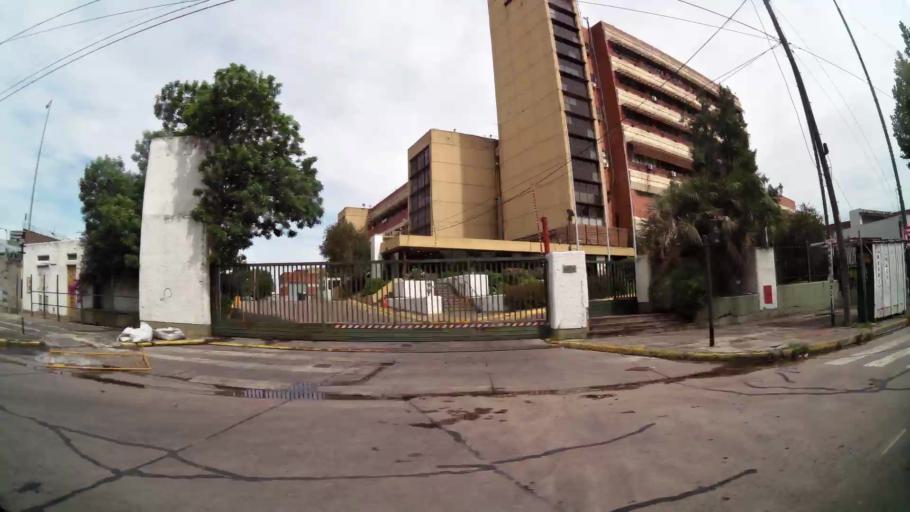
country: AR
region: Buenos Aires F.D.
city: Villa Lugano
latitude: -34.6655
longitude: -58.4389
